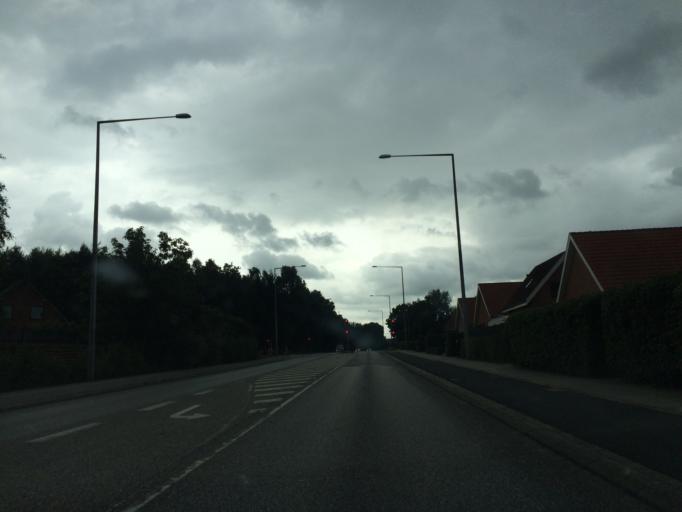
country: DK
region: Central Jutland
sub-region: Silkeborg Kommune
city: Silkeborg
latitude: 56.1767
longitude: 9.5292
